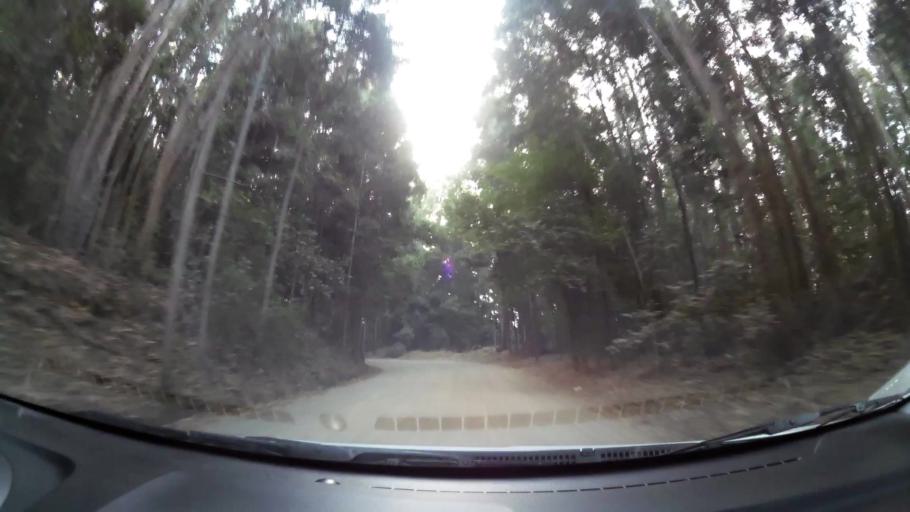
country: CL
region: Biobio
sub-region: Provincia de Concepcion
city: Concepcion
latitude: -36.8544
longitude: -73.0860
